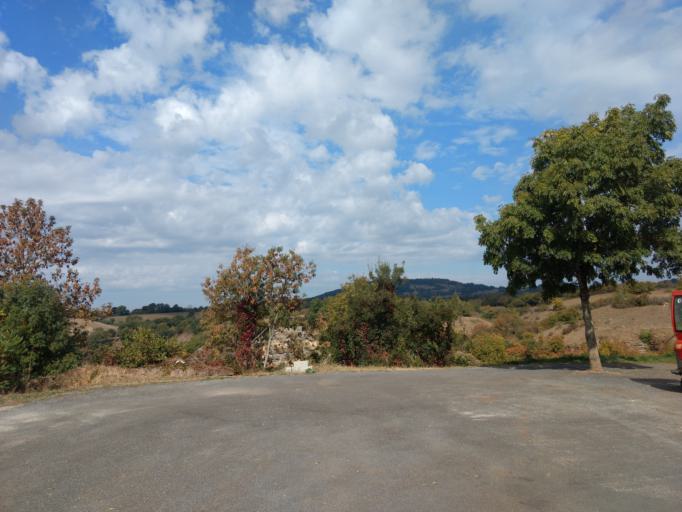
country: FR
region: Midi-Pyrenees
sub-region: Departement de l'Aveyron
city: Bozouls
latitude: 44.4689
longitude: 2.7146
